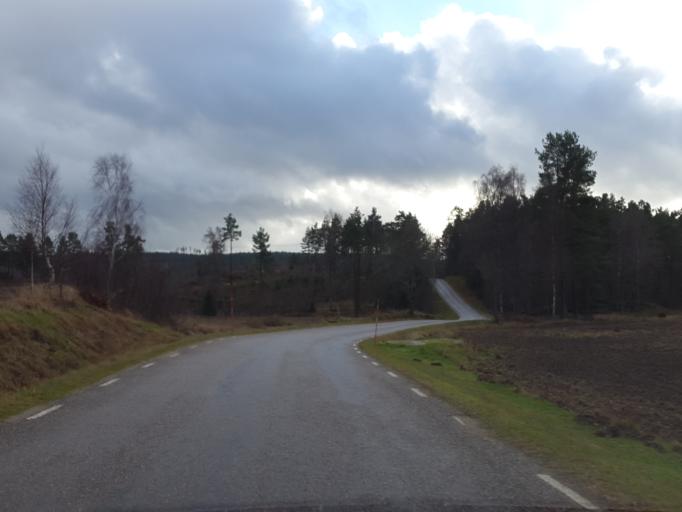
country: SE
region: Vaestra Goetaland
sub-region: Vargarda Kommun
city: Jonstorp
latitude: 57.9933
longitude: 12.7695
